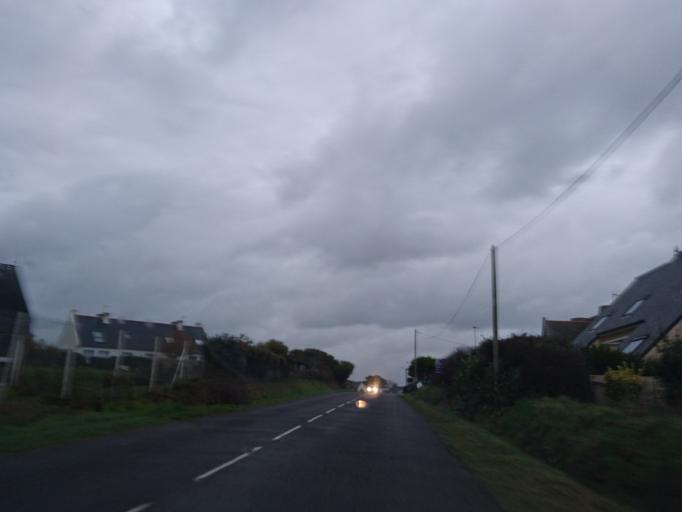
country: FR
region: Brittany
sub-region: Departement du Finistere
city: Le Conquet
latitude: 48.3537
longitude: -4.7771
